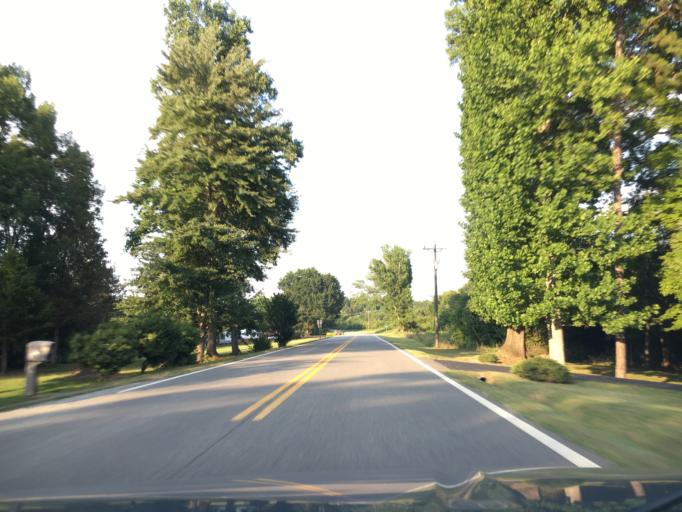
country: US
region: Virginia
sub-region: Halifax County
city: Mountain Road
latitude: 36.8284
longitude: -79.0873
